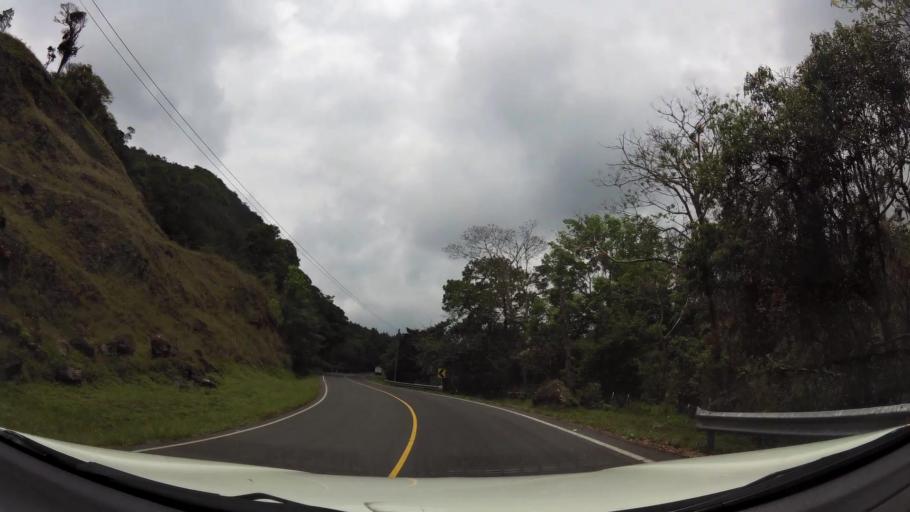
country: NI
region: Matagalpa
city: Matagalpa
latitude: 12.9921
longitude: -85.9183
